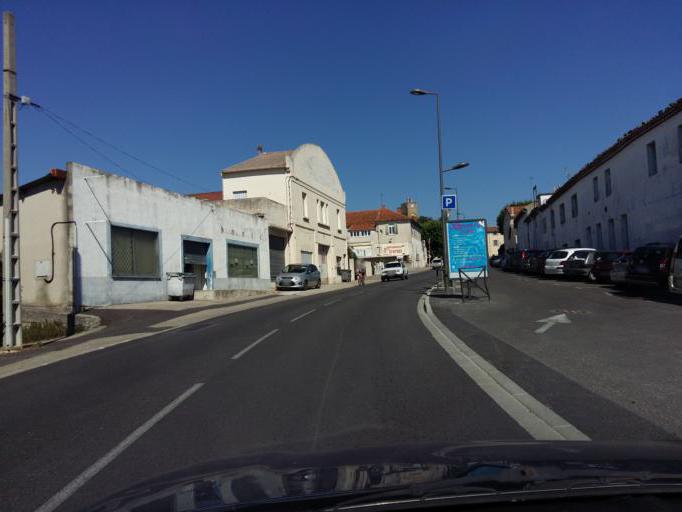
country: FR
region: Provence-Alpes-Cote d'Azur
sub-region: Departement du Vaucluse
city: Valreas
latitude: 44.3847
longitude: 4.9859
